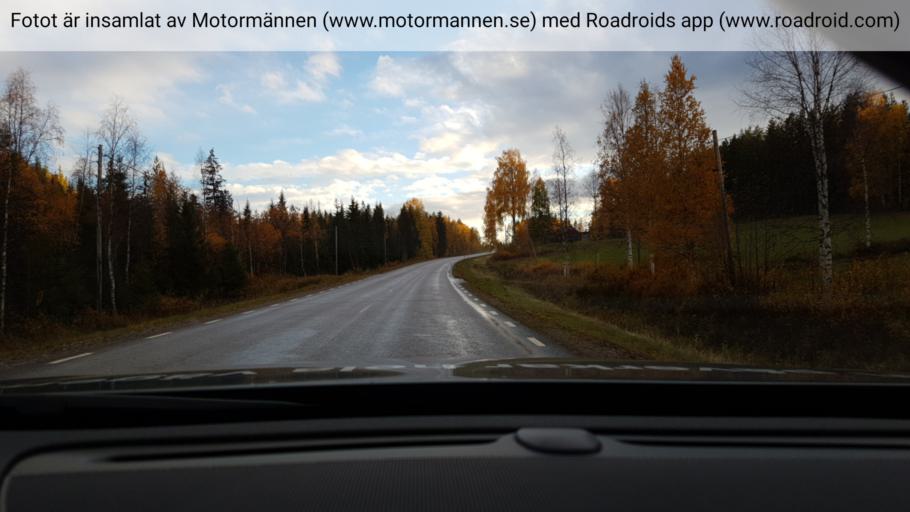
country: SE
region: Norrbotten
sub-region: Overkalix Kommun
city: OEverkalix
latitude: 66.7349
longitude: 22.6690
